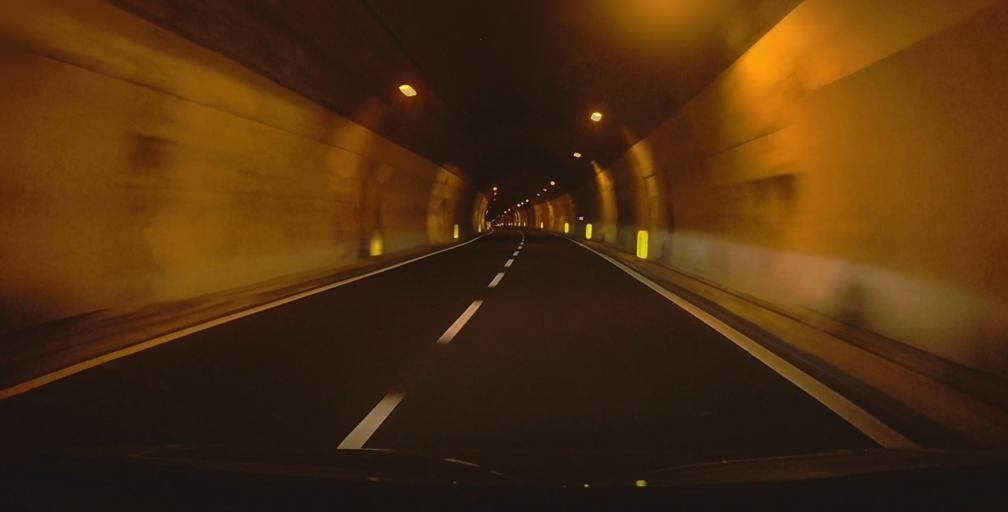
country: IT
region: Sicily
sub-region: Messina
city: Forza d'Agro
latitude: 37.9100
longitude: 15.3388
